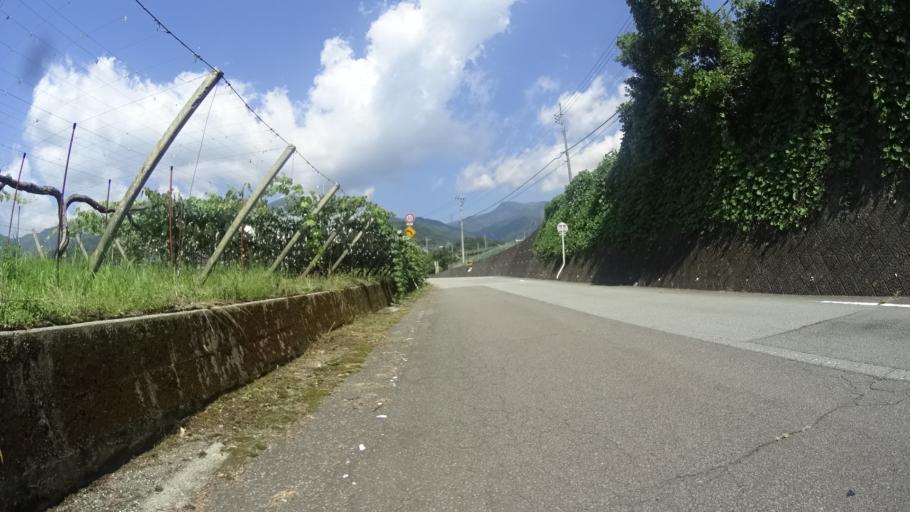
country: JP
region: Yamanashi
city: Enzan
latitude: 35.7562
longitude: 138.7105
